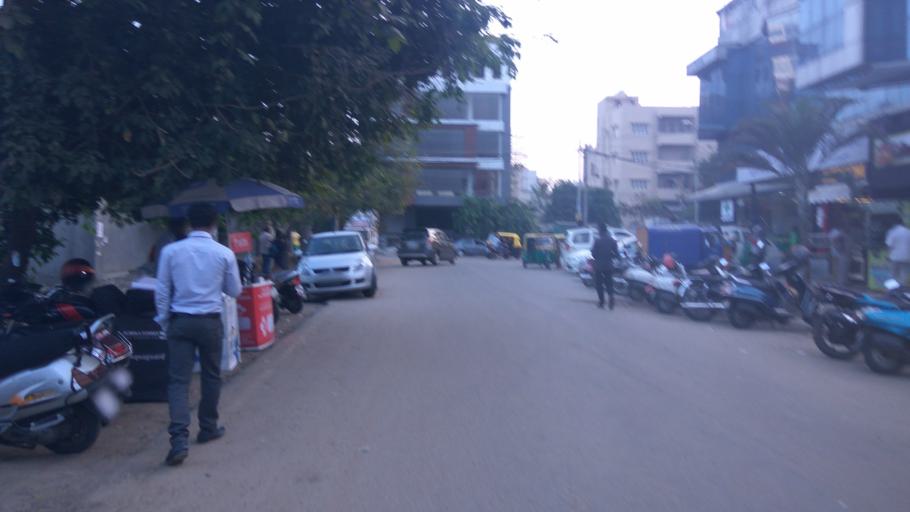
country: IN
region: Karnataka
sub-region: Bangalore Urban
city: Bangalore
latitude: 12.9128
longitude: 77.6368
